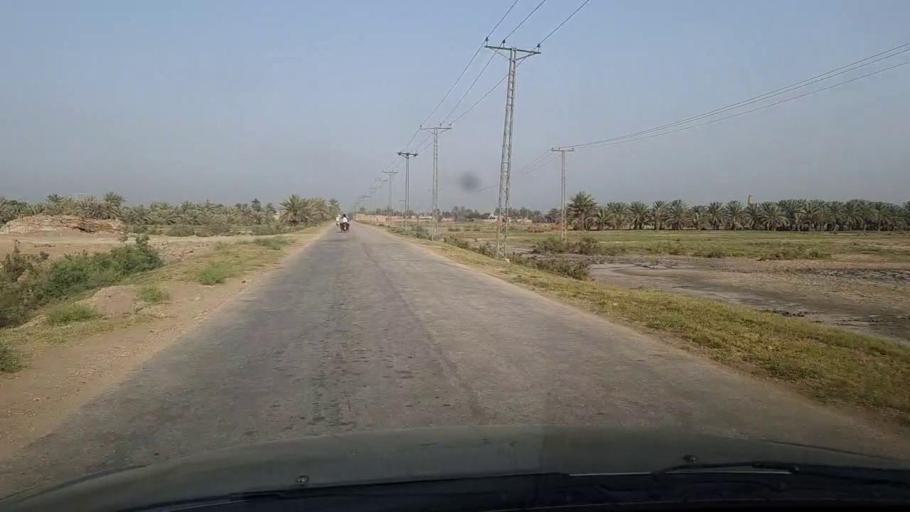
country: PK
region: Sindh
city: Pir jo Goth
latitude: 27.5694
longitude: 68.6336
